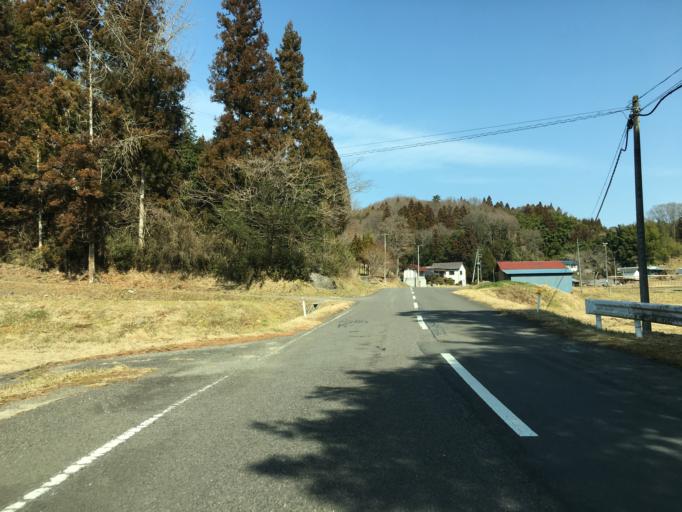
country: JP
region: Fukushima
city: Ishikawa
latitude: 37.0987
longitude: 140.4529
